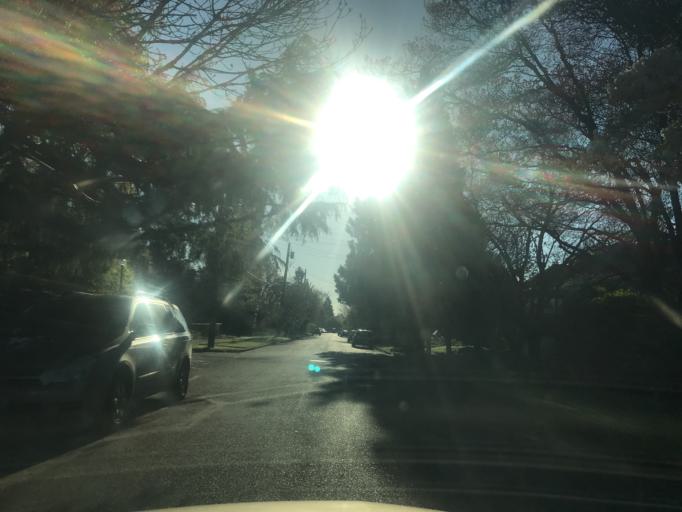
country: US
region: Oregon
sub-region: Multnomah County
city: Lents
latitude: 45.4961
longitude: -122.6049
